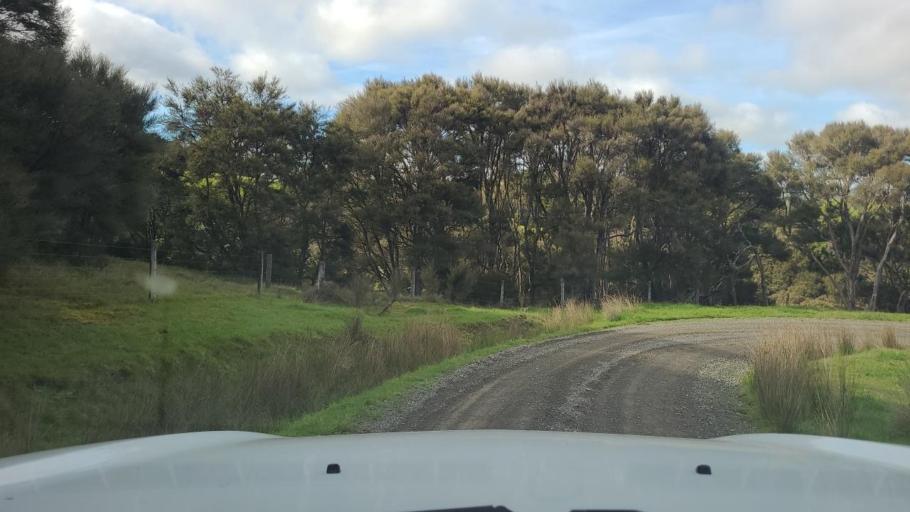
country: NZ
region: Wellington
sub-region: South Wairarapa District
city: Waipawa
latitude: -41.2611
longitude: 175.6932
